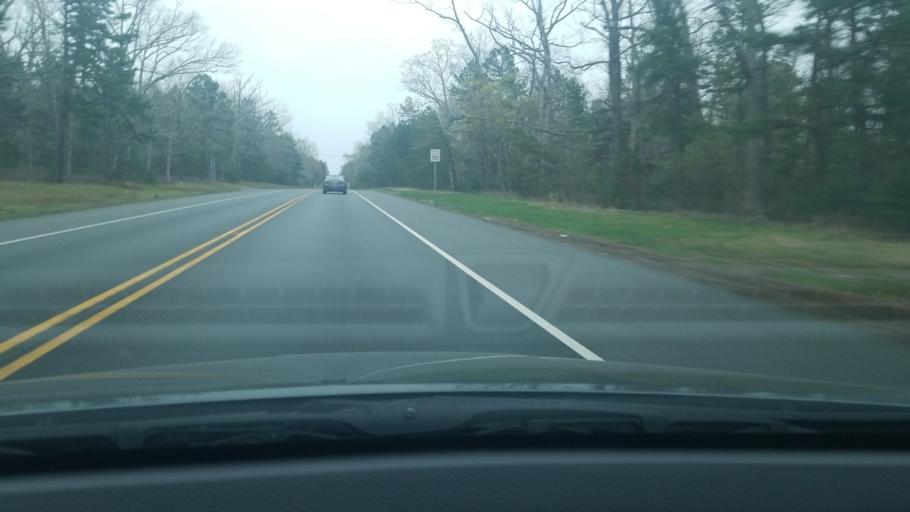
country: US
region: New Jersey
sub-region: Burlington County
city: Leisuretowne
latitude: 39.8889
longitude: -74.6533
